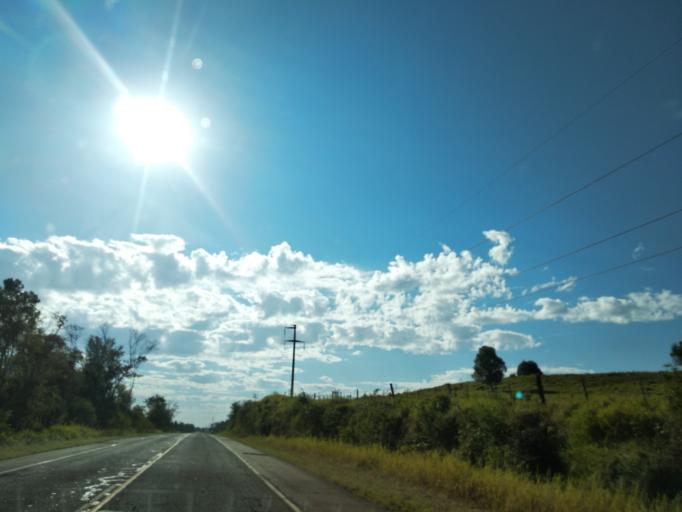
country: AR
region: Misiones
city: Aristobulo del Valle
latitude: -27.0757
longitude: -54.9875
